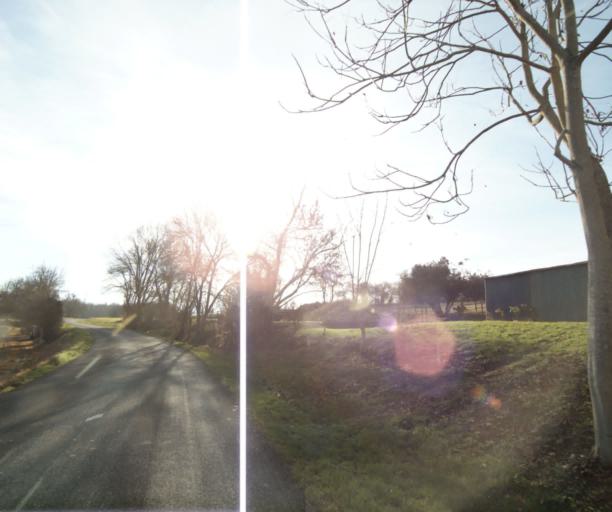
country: FR
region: Poitou-Charentes
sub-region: Departement de la Charente-Maritime
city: Chaniers
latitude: 45.7222
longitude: -0.5212
